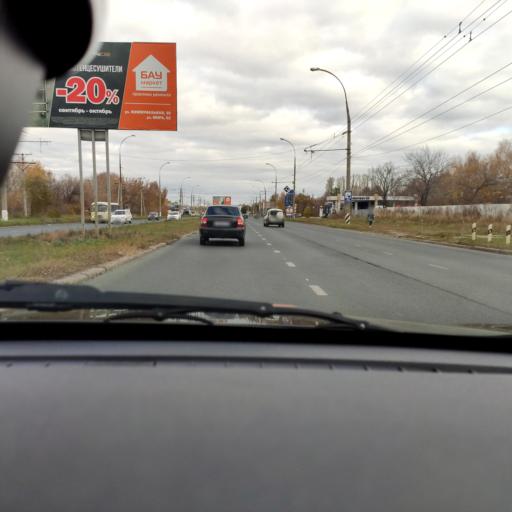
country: RU
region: Samara
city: Tol'yatti
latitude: 53.5483
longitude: 49.3065
